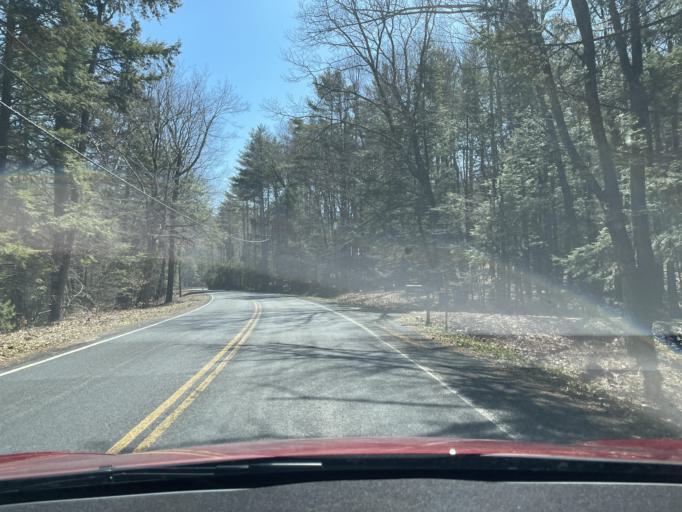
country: US
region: New York
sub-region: Ulster County
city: Shokan
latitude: 42.0215
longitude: -74.1915
